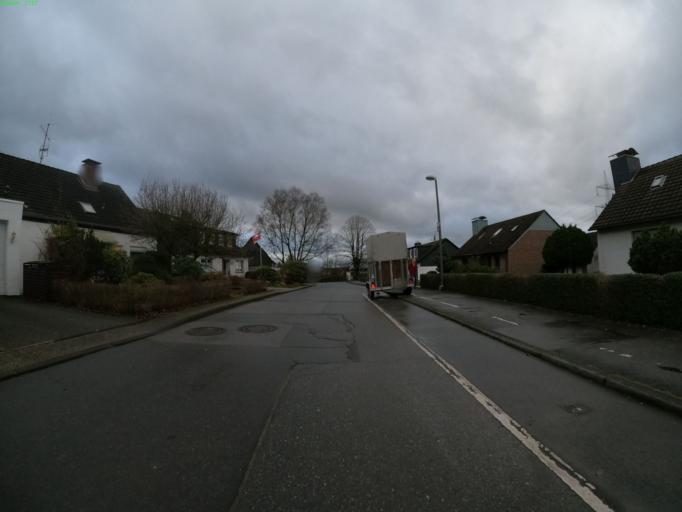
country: DE
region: North Rhine-Westphalia
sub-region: Regierungsbezirk Dusseldorf
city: Solingen
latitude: 51.1830
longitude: 7.1356
